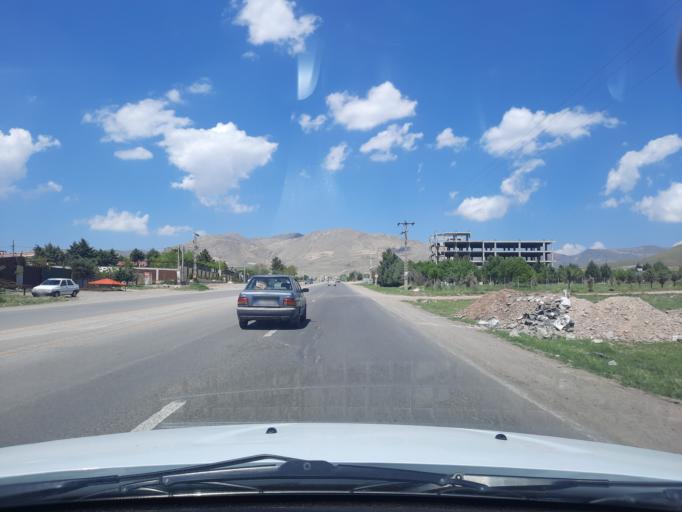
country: IR
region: Qazvin
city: Qazvin
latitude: 36.3194
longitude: 50.1469
